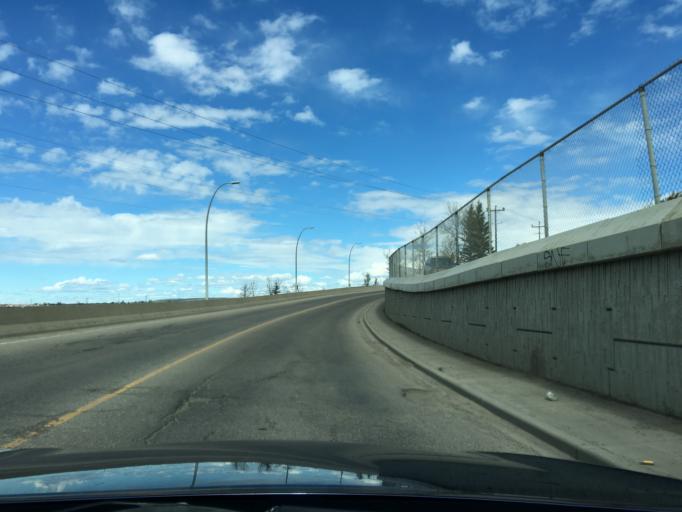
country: CA
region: Alberta
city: Calgary
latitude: 51.0389
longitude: -114.0010
